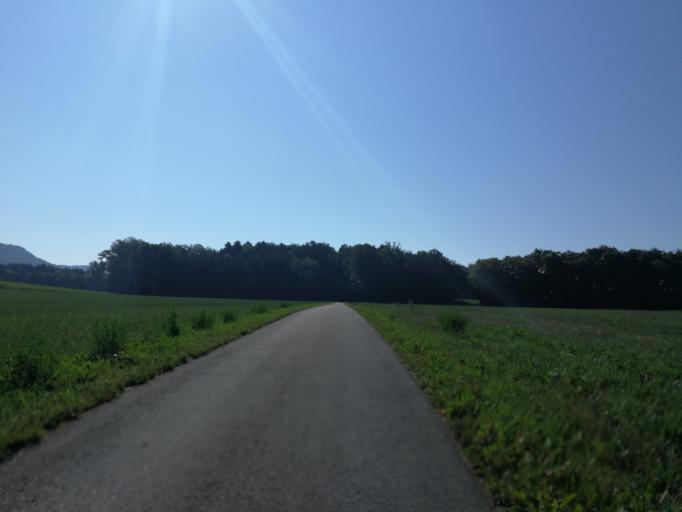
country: CH
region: Thurgau
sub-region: Frauenfeld District
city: Wagenhausen
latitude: 47.6724
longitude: 8.8187
